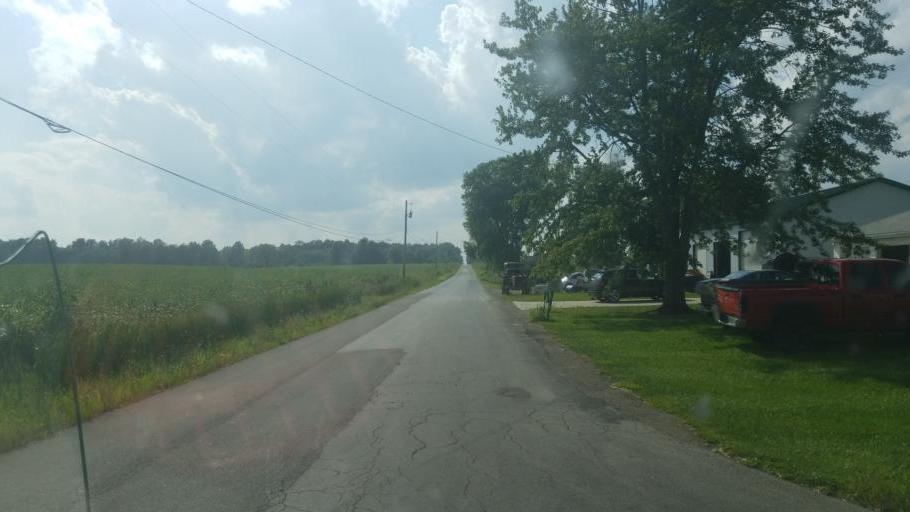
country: US
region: Ohio
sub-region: Wayne County
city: West Salem
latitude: 40.9524
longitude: -82.0536
